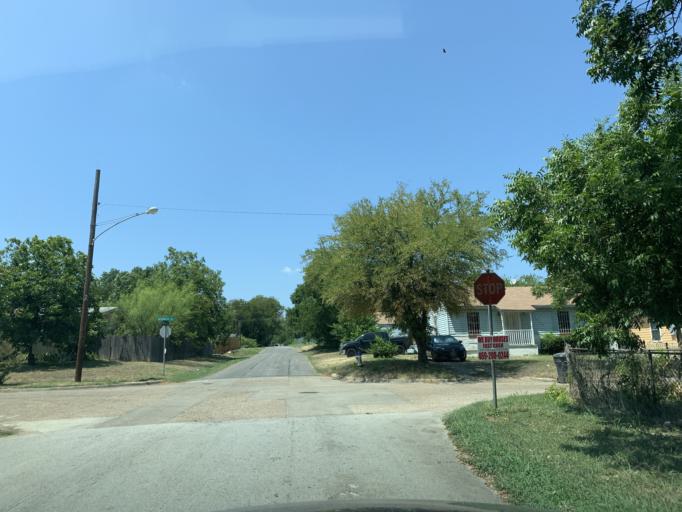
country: US
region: Texas
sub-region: Dallas County
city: Dallas
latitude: 32.6864
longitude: -96.8025
